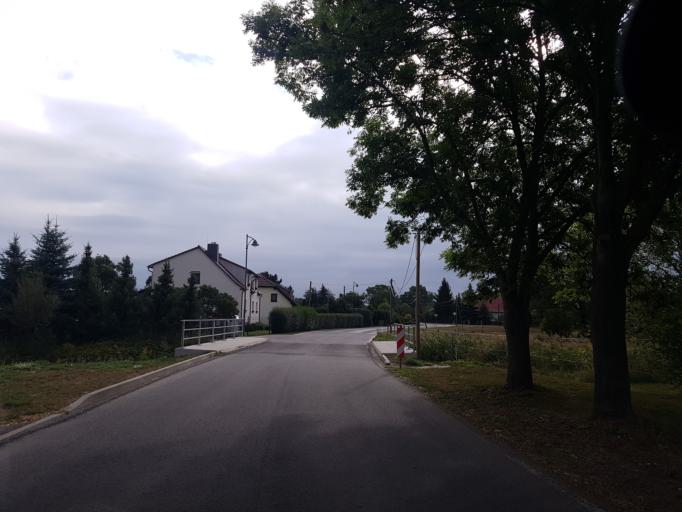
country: DE
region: Brandenburg
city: Calau
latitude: 51.7734
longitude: 13.8768
